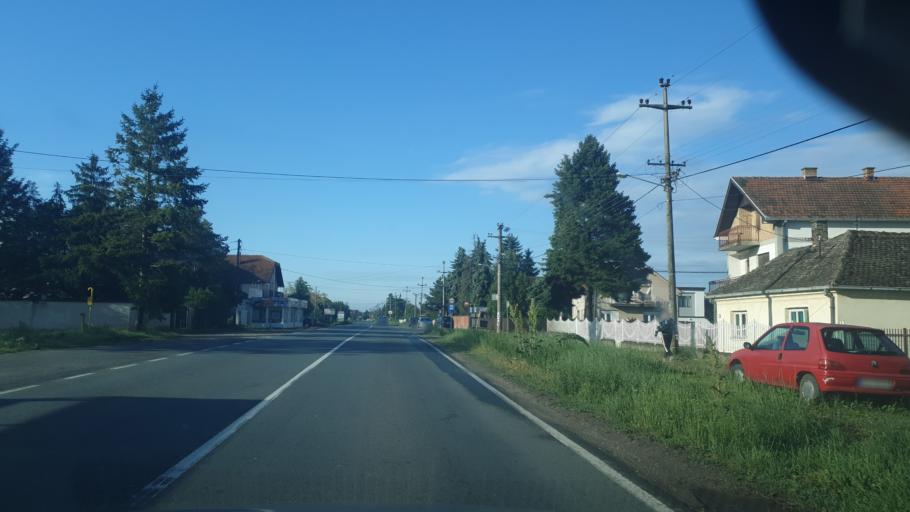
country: RS
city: Zvecka
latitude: 44.6369
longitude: 20.1827
